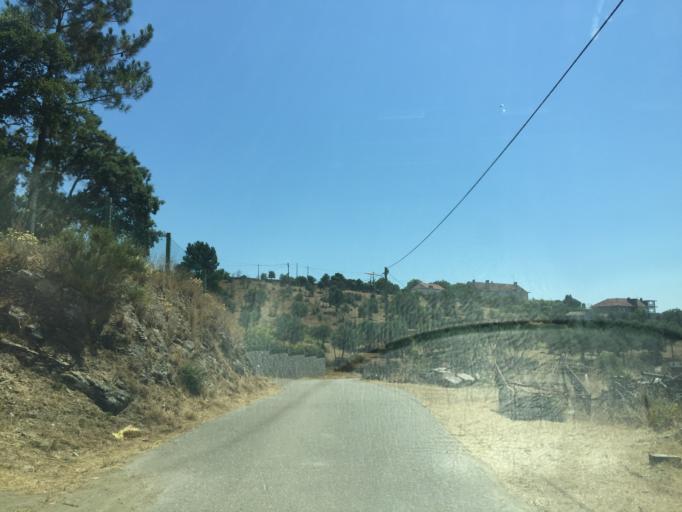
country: PT
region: Santarem
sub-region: Constancia
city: Constancia
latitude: 39.5741
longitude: -8.2972
